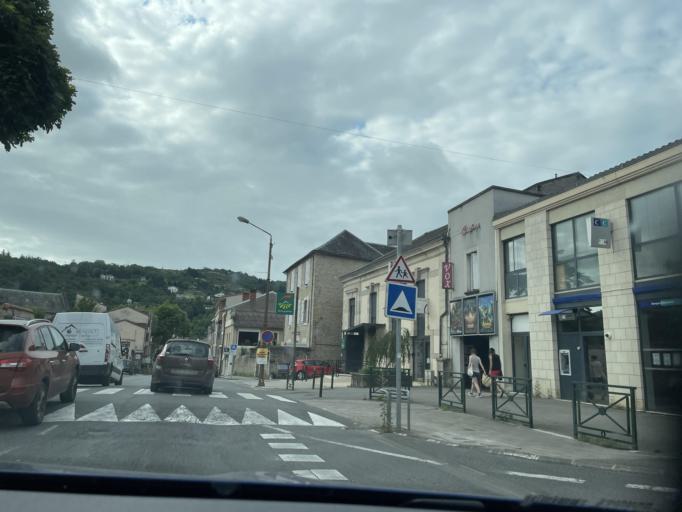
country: FR
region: Midi-Pyrenees
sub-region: Departement de l'Aveyron
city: Villefranche-de-Rouergue
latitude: 44.3515
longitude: 2.0345
